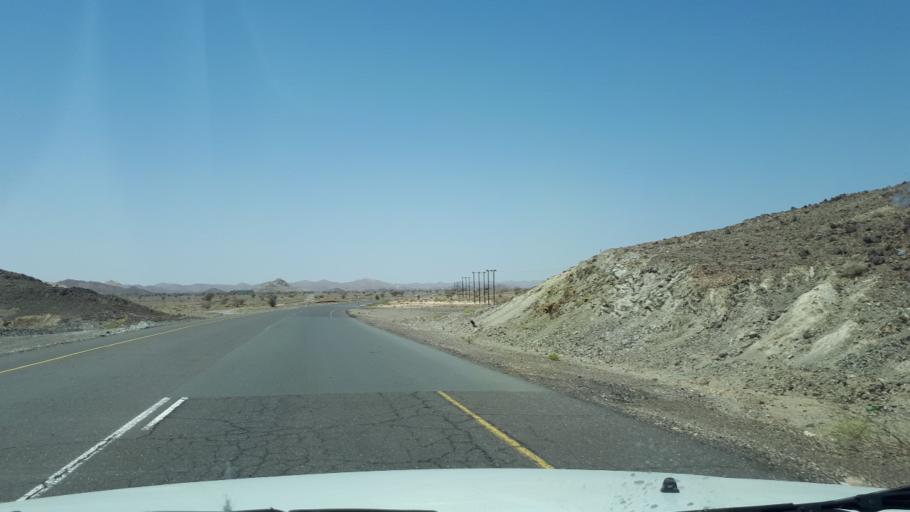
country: OM
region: Ash Sharqiyah
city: Ibra'
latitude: 22.6275
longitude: 58.4559
